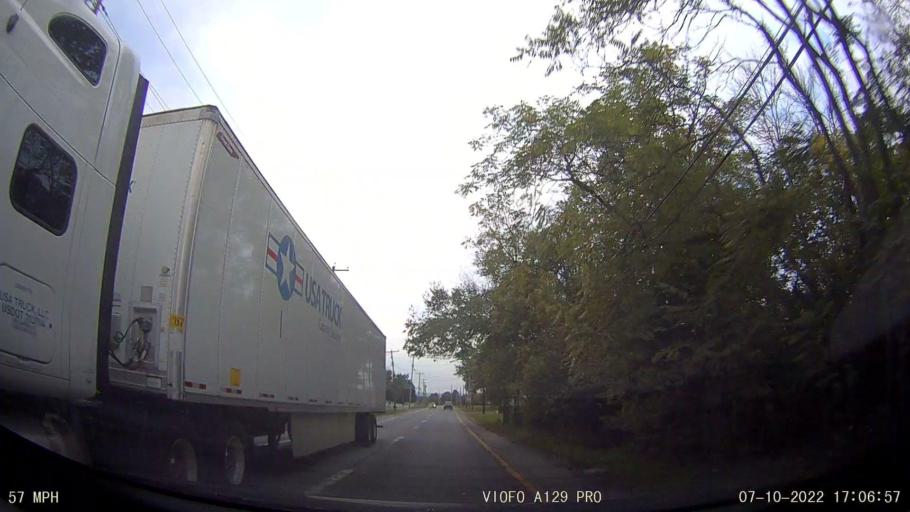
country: US
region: Pennsylvania
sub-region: Berks County
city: Birdsboro
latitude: 40.2842
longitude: -75.8100
